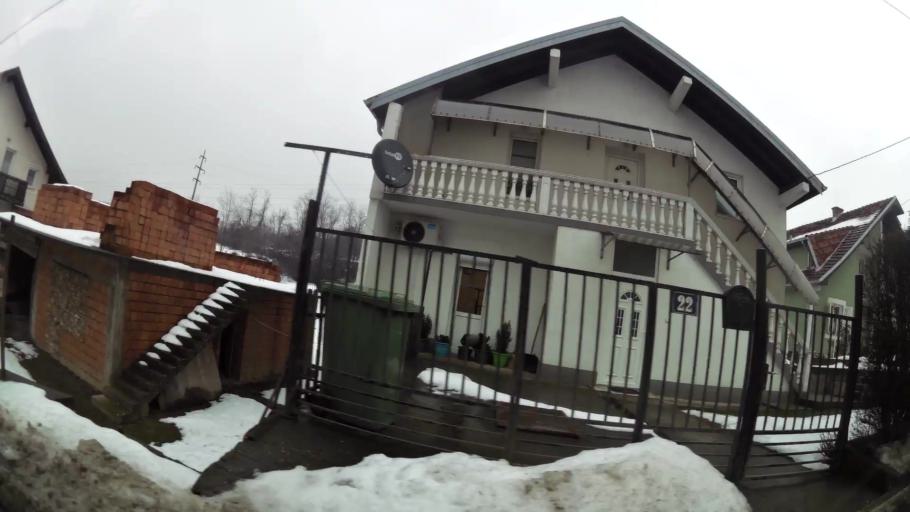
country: RS
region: Central Serbia
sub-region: Belgrade
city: Zvezdara
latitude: 44.7631
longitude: 20.5248
